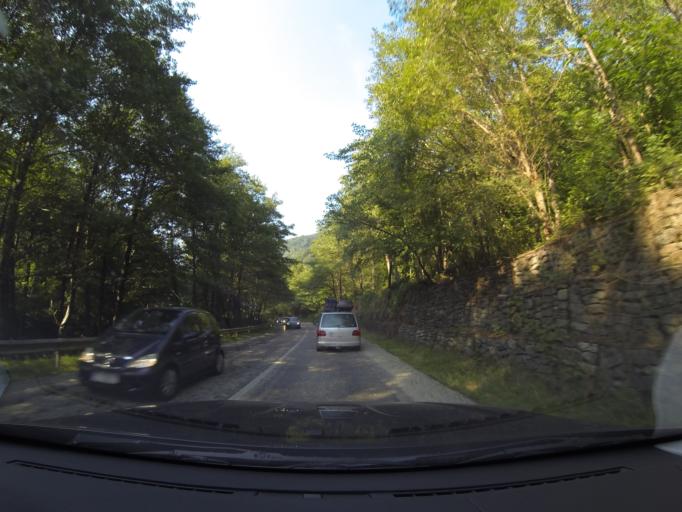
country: RO
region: Arges
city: Poenari
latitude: 45.3381
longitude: 24.6364
